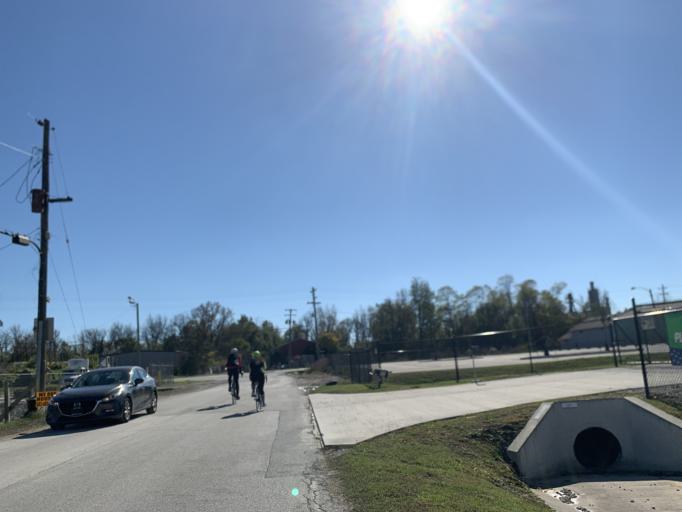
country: US
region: Kentucky
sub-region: Jefferson County
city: Shively
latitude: 38.2171
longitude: -85.8129
